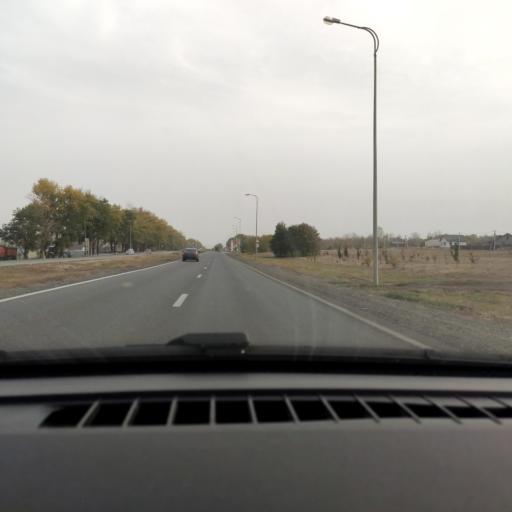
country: RU
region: Belgorod
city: Razumnoye
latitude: 50.6576
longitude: 36.6961
